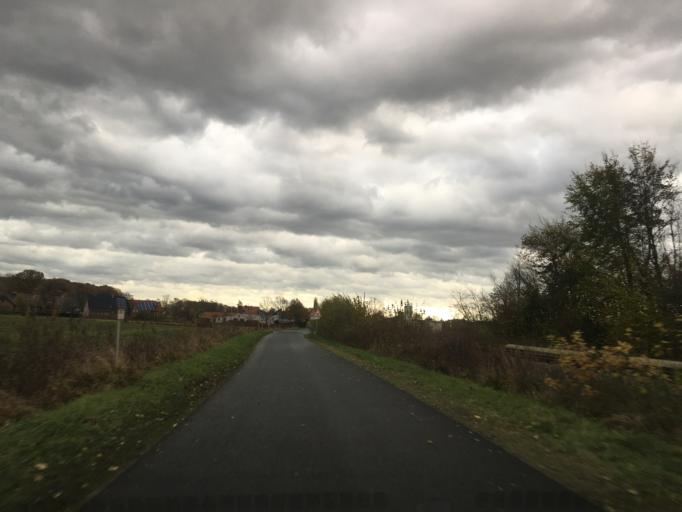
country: DE
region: North Rhine-Westphalia
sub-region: Regierungsbezirk Munster
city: Greven
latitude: 52.0236
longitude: 7.5570
